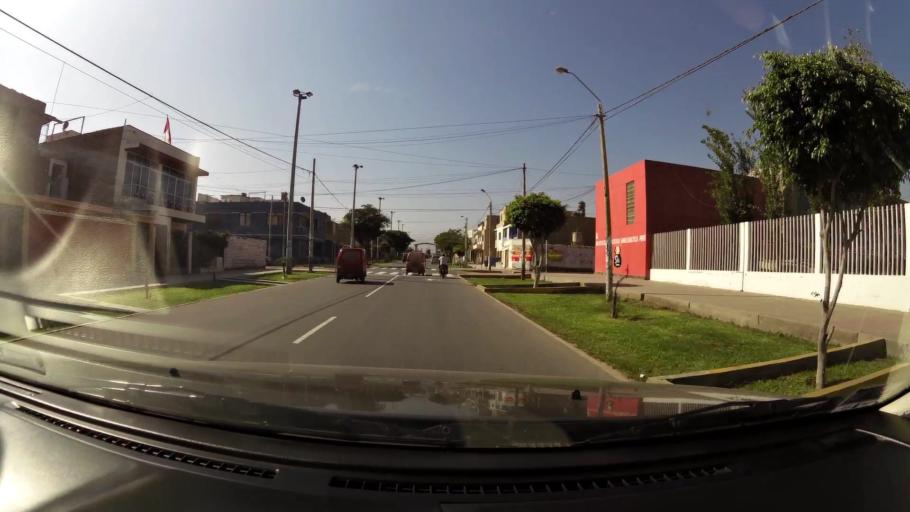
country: PE
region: Ica
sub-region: Provincia de Chincha
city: Chincha Alta
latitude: -13.4121
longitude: -76.1302
